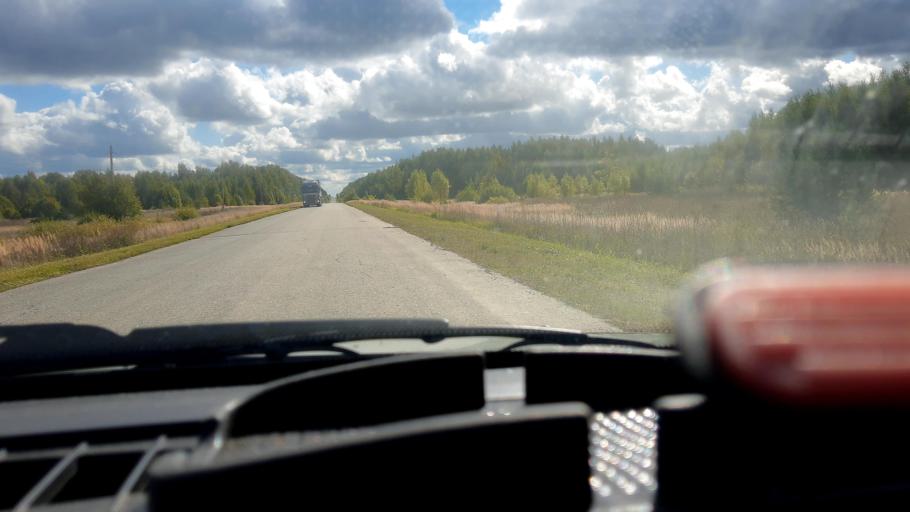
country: RU
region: Mariy-El
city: Kilemary
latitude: 56.9329
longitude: 46.6991
